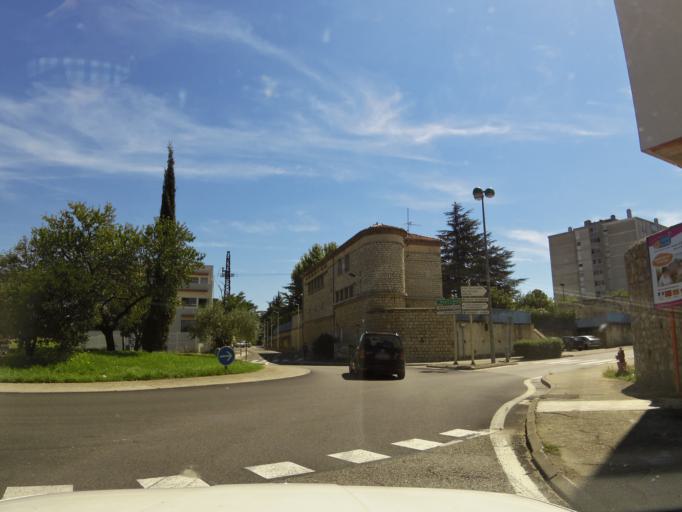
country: FR
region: Languedoc-Roussillon
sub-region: Departement du Gard
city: Bagnols-sur-Ceze
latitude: 44.1671
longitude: 4.6118
